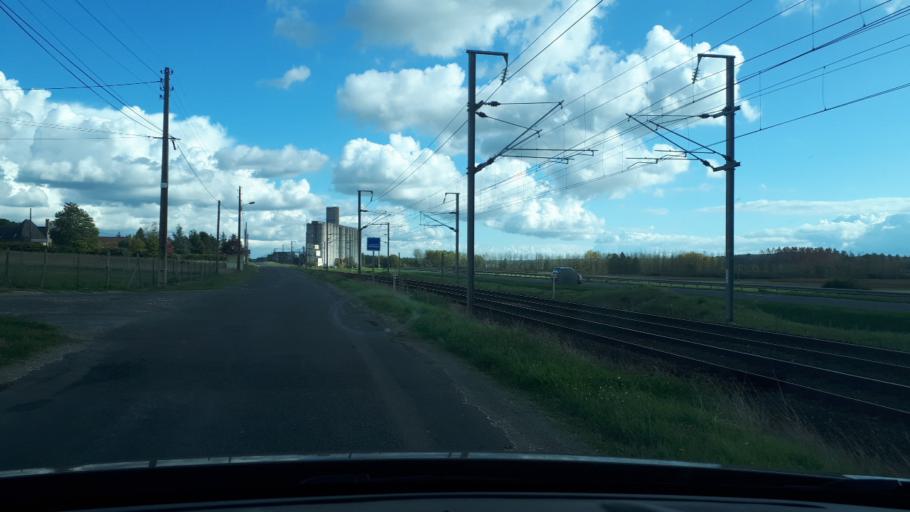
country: FR
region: Centre
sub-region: Departement du Loir-et-Cher
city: Mareuil-sur-Cher
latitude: 47.2997
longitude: 1.3559
